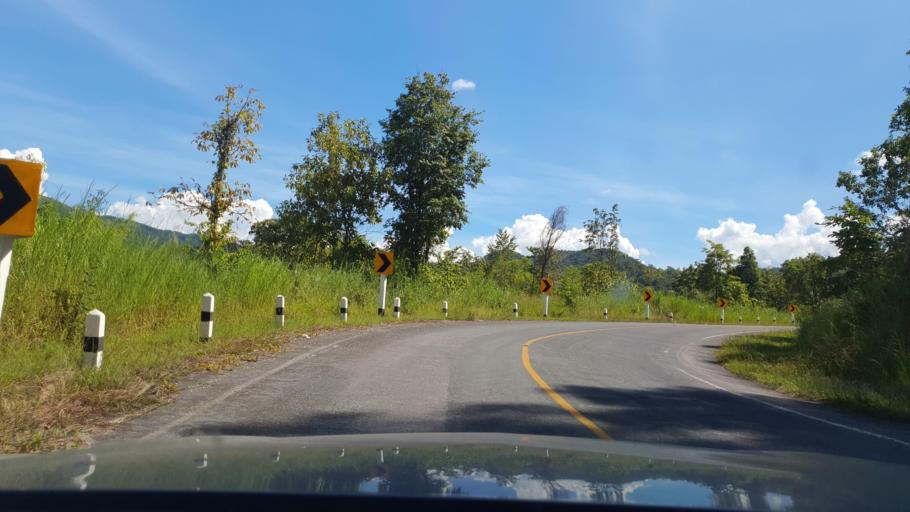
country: TH
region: Chiang Mai
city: Phrao
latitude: 19.3611
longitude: 99.2750
